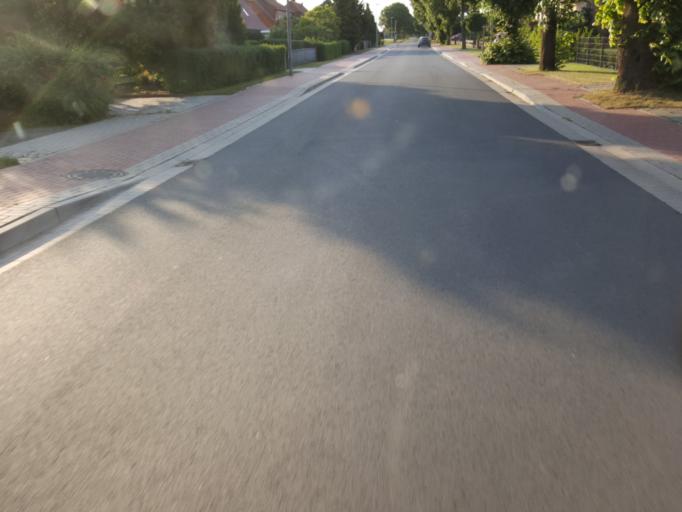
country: DE
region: Lower Saxony
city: Landesbergen
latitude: 52.5519
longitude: 9.1283
